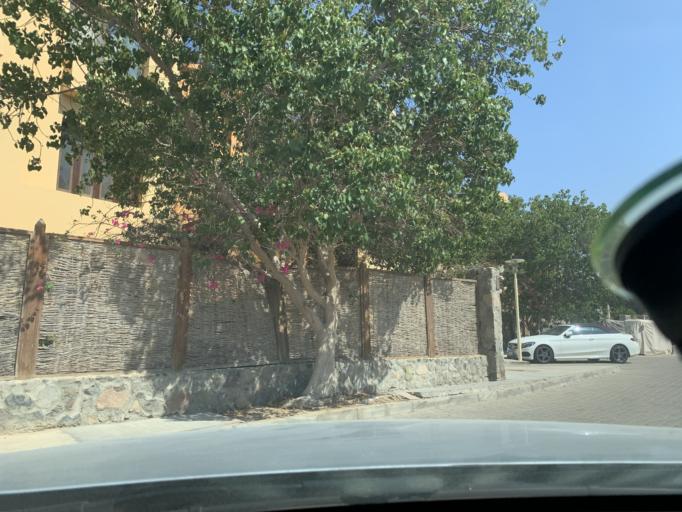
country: EG
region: Red Sea
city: El Gouna
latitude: 27.4015
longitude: 33.6715
